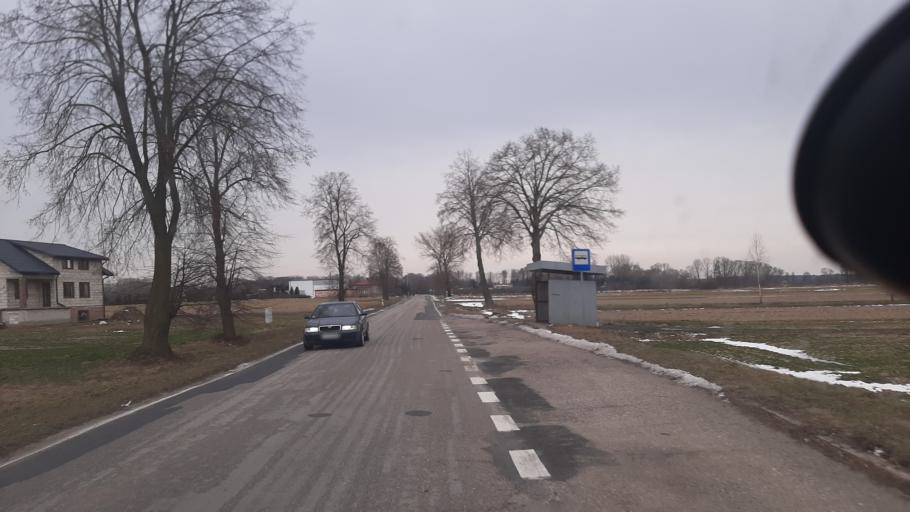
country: PL
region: Lublin Voivodeship
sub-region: Powiat lubartowski
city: Kamionka
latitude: 51.4532
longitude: 22.4212
